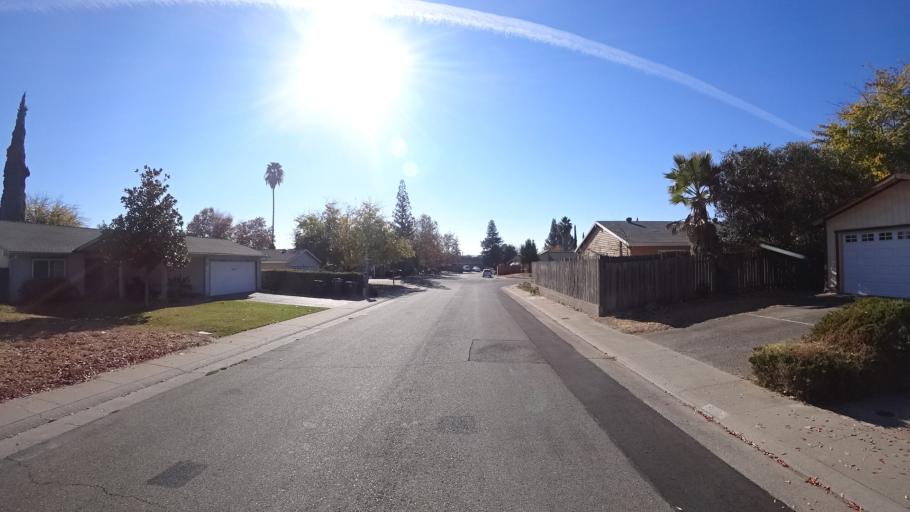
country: US
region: California
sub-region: Sacramento County
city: Antelope
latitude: 38.7121
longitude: -121.3122
